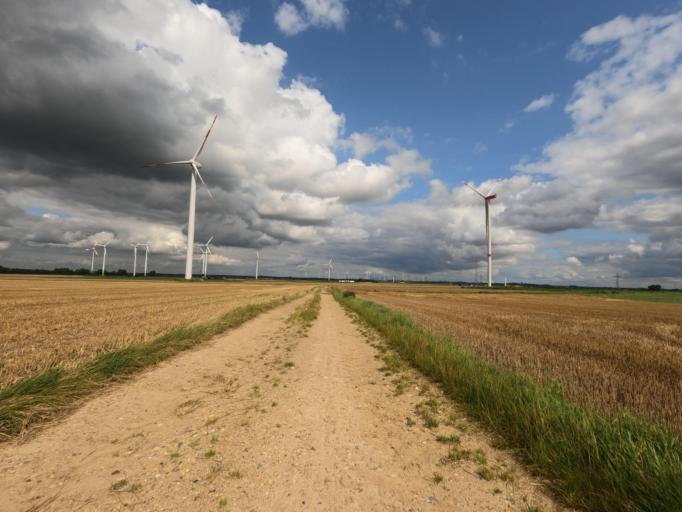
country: DE
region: North Rhine-Westphalia
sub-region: Regierungsbezirk Koln
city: Linnich
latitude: 50.9806
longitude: 6.2239
